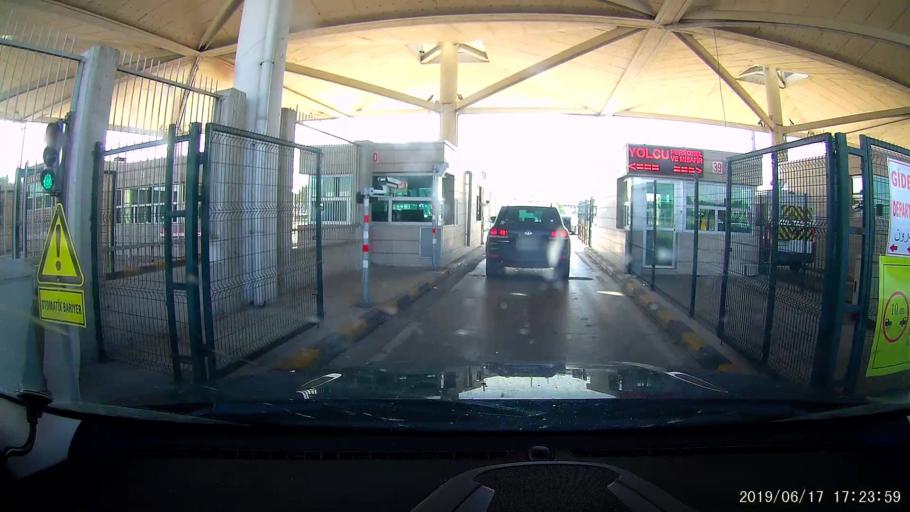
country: GR
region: East Macedonia and Thrace
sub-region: Nomos Evrou
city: Rizia
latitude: 41.7147
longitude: 26.3629
